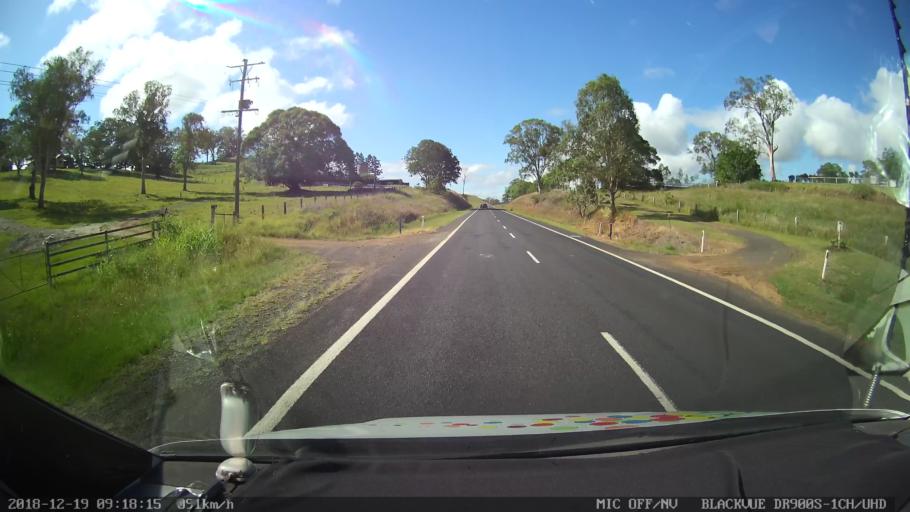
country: AU
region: New South Wales
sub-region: Kyogle
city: Kyogle
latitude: -28.5446
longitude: 152.9772
